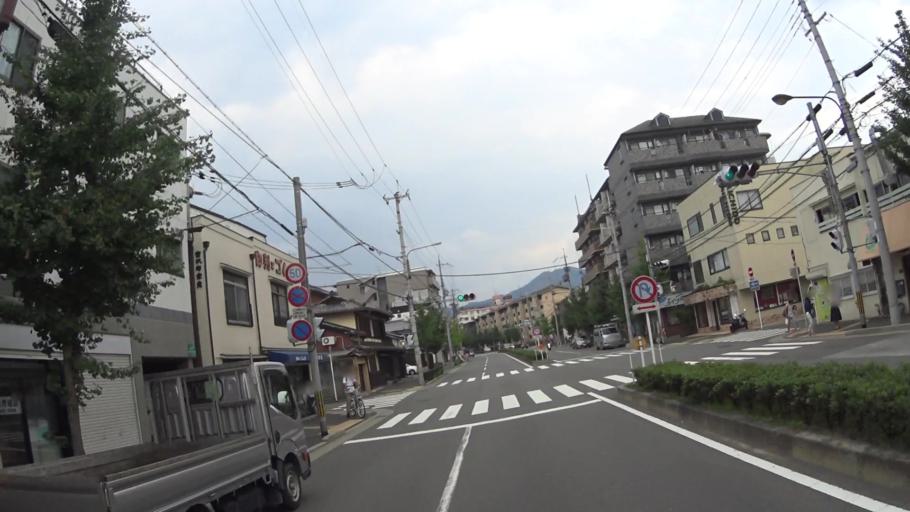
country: JP
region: Kyoto
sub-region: Kyoto-shi
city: Kamigyo-ku
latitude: 35.0288
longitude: 135.7739
